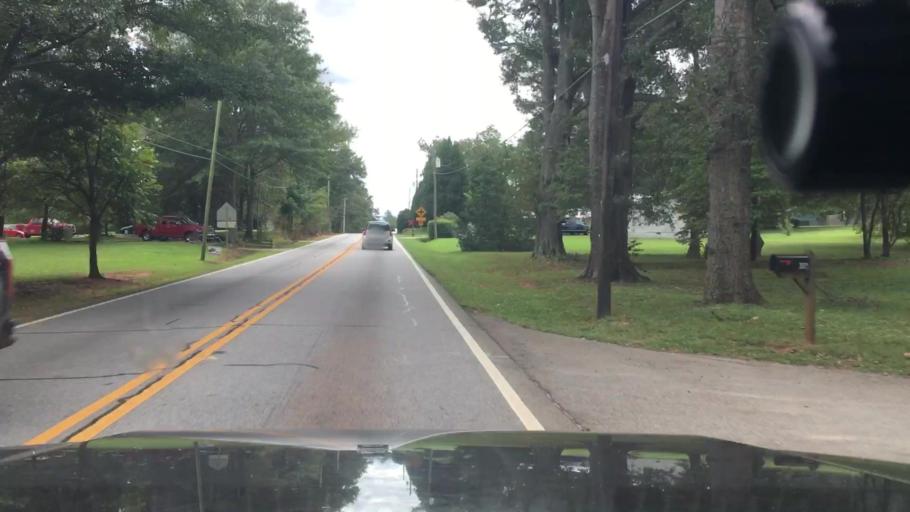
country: US
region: Georgia
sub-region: Coweta County
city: East Newnan
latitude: 33.2840
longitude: -84.7668
